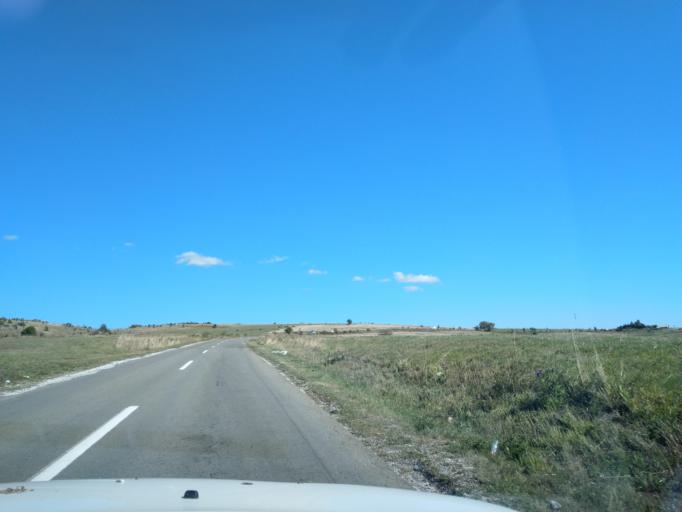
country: RS
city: Sokolovica
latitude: 43.2763
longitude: 20.2143
